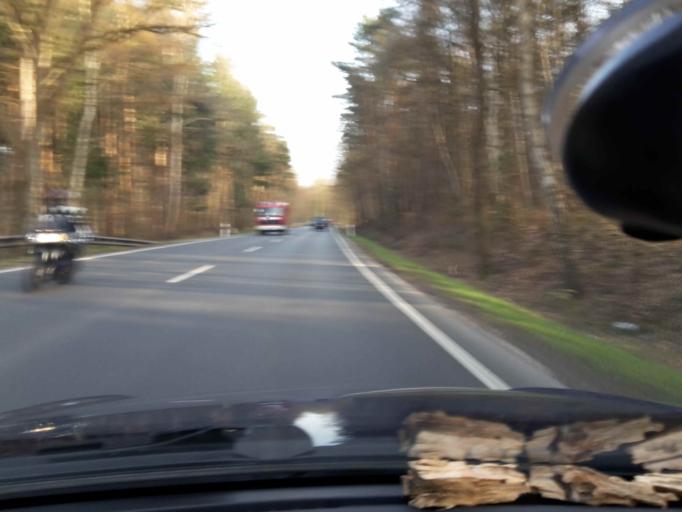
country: DE
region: Lower Saxony
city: Buxtehude
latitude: 53.4770
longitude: 9.6466
